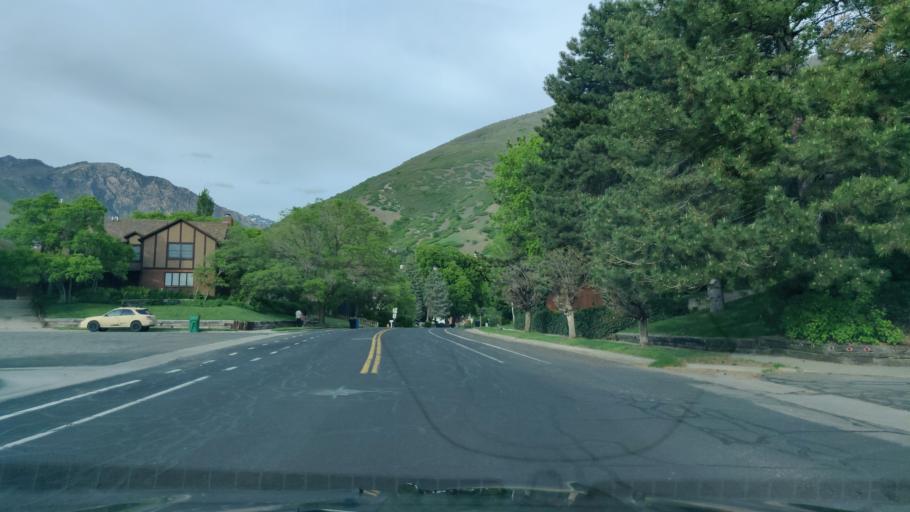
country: US
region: Utah
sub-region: Salt Lake County
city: Cottonwood Heights
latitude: 40.6045
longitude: -111.7981
